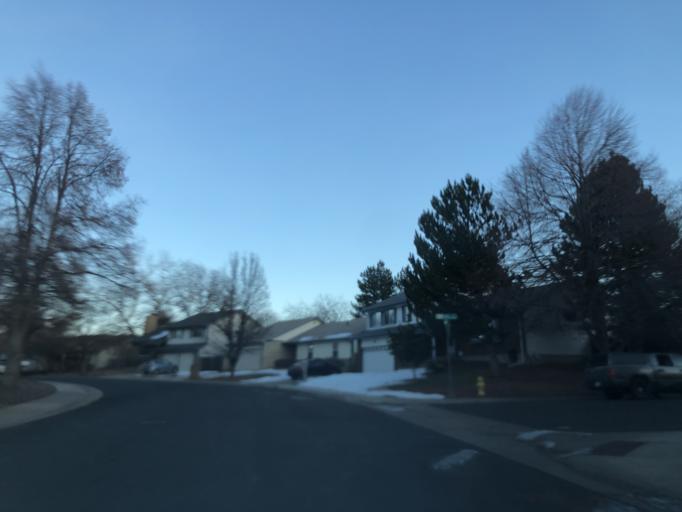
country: US
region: Colorado
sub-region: Adams County
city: Aurora
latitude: 39.7041
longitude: -104.8007
